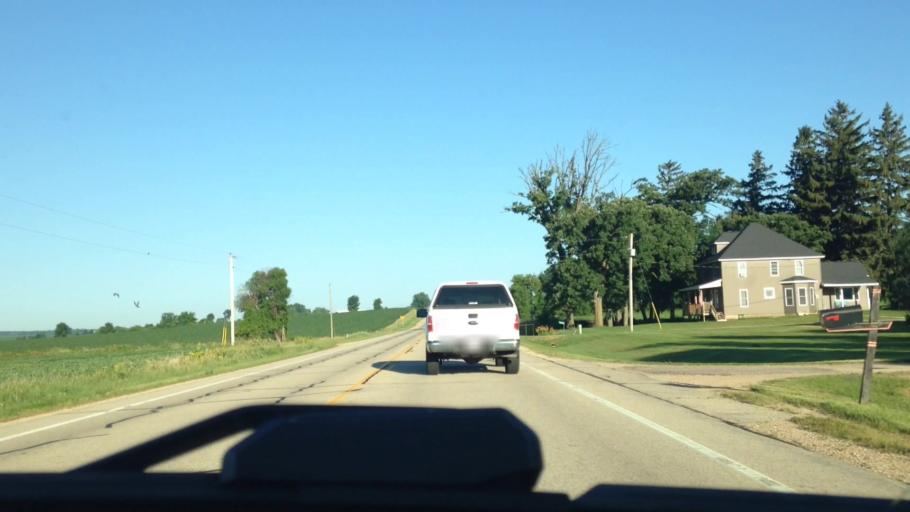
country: US
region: Wisconsin
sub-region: Columbia County
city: Rio
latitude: 43.3406
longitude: -89.1834
